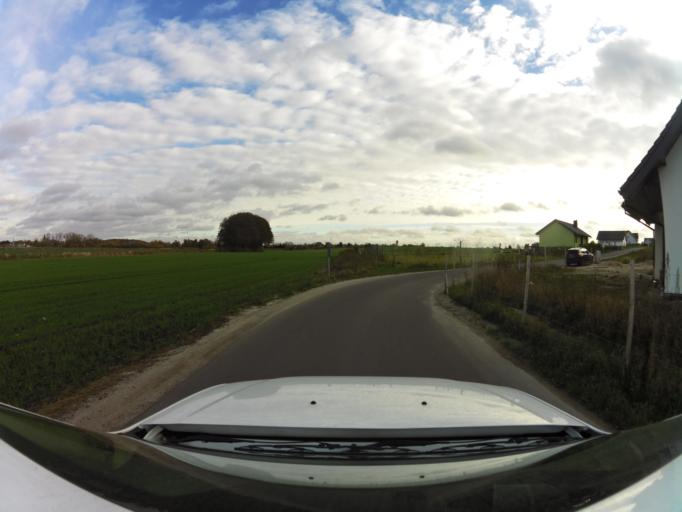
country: PL
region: West Pomeranian Voivodeship
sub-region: Powiat gryficki
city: Gryfice
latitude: 53.9102
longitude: 15.1755
